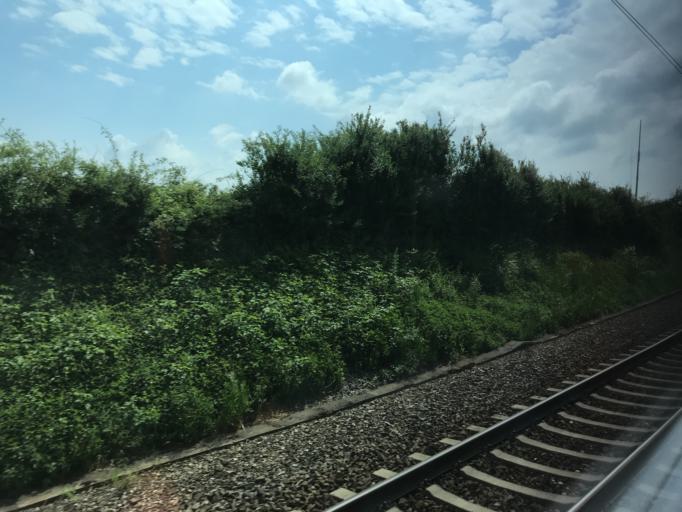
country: DE
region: Baden-Wuerttemberg
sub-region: Tuebingen Region
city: Beimerstetten
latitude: 48.4561
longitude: 9.9757
